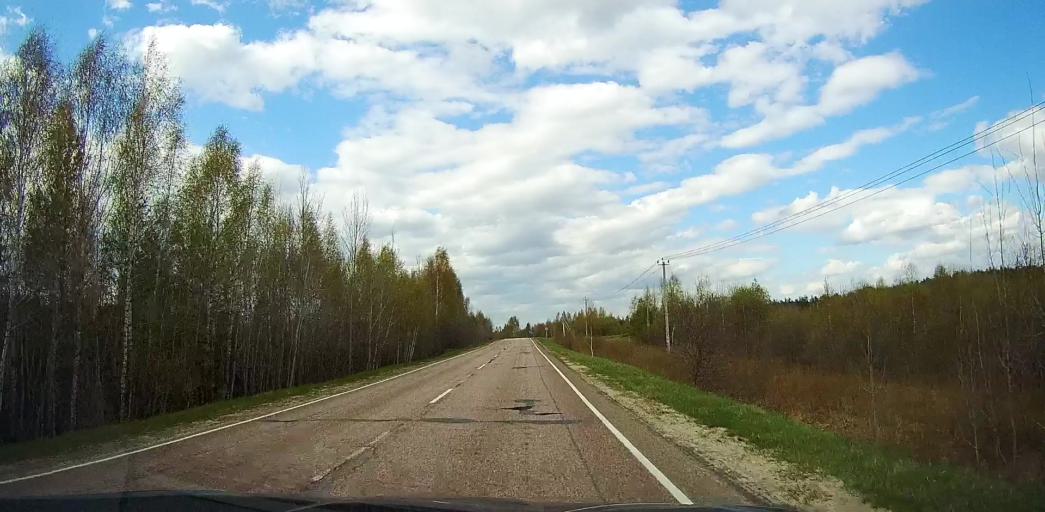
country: RU
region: Moskovskaya
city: Rakhmanovo
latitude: 55.6749
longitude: 38.6453
